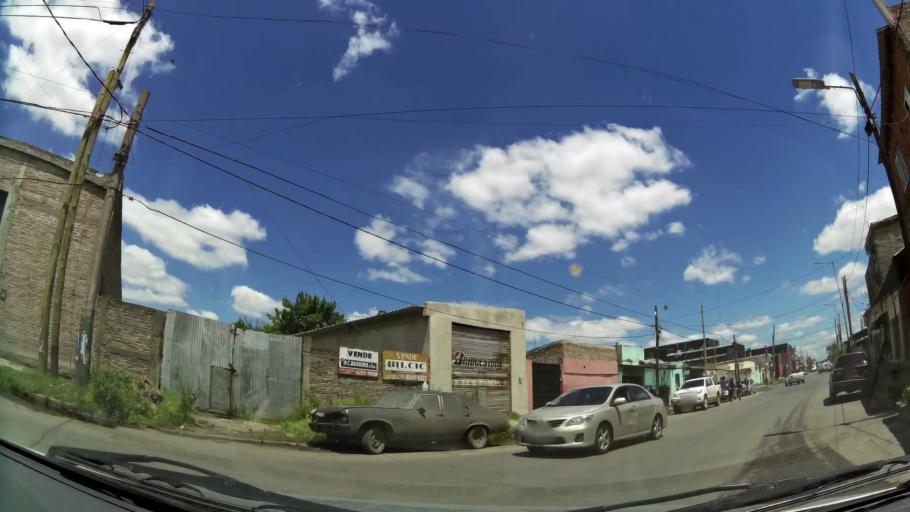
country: AR
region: Buenos Aires
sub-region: Partido de Lanus
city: Lanus
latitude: -34.7157
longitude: -58.4324
